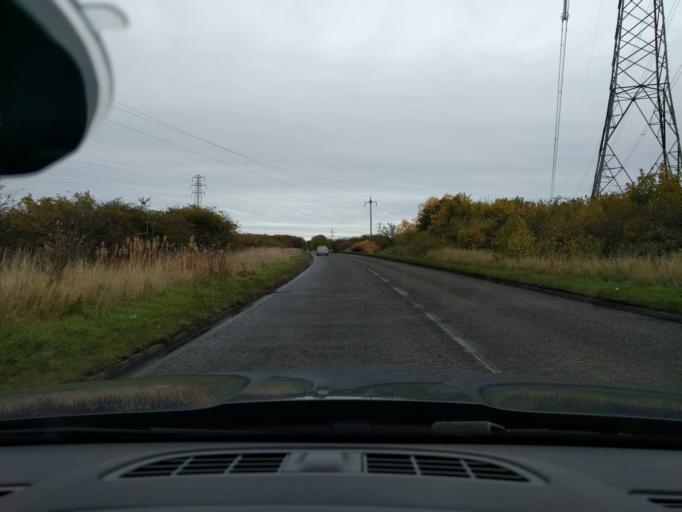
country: GB
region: England
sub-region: Northumberland
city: Blyth
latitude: 55.1451
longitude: -1.5430
